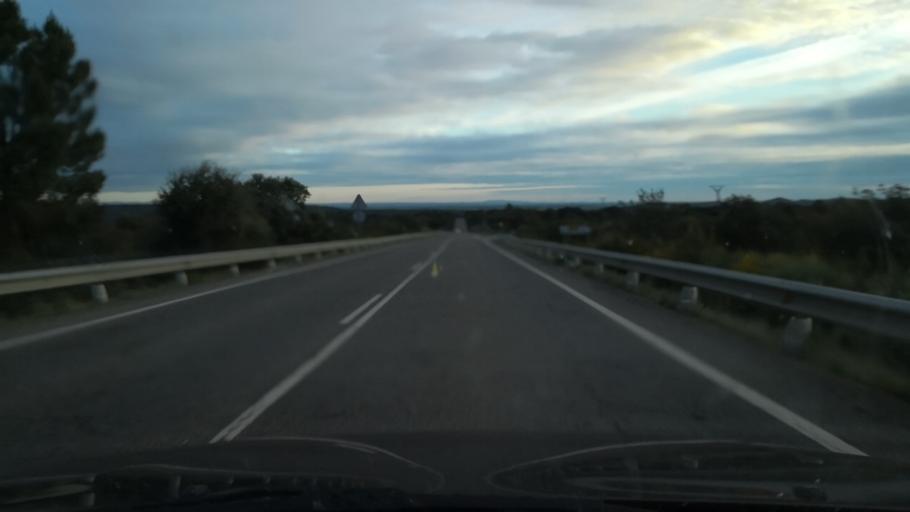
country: ES
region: Extremadura
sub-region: Provincia de Badajoz
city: Puebla de Obando
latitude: 39.1600
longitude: -6.6424
